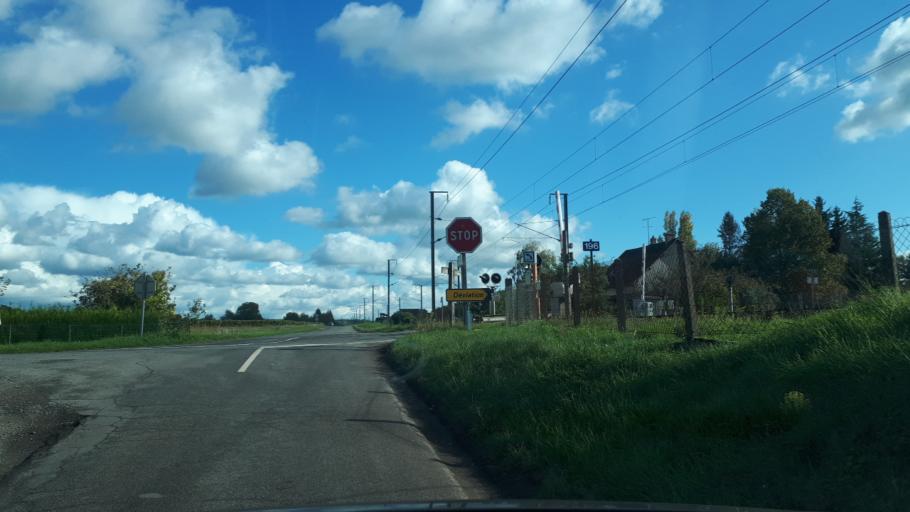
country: FR
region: Centre
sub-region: Departement du Loir-et-Cher
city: Thesee
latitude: 47.3192
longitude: 1.3218
